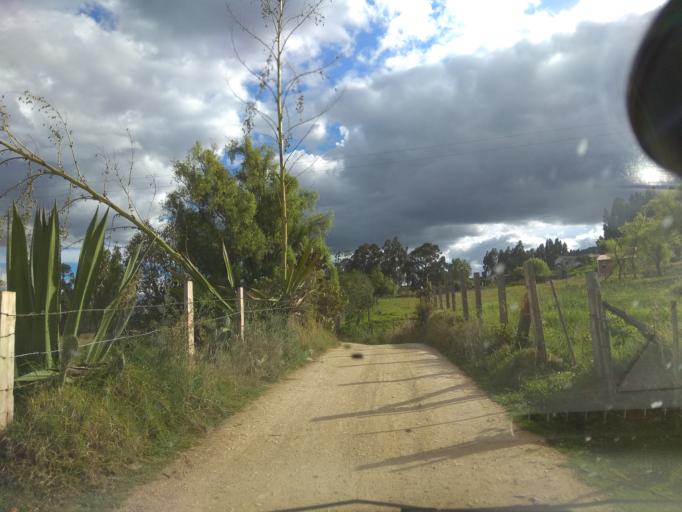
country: CO
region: Boyaca
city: Duitama
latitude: 5.8285
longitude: -73.0812
